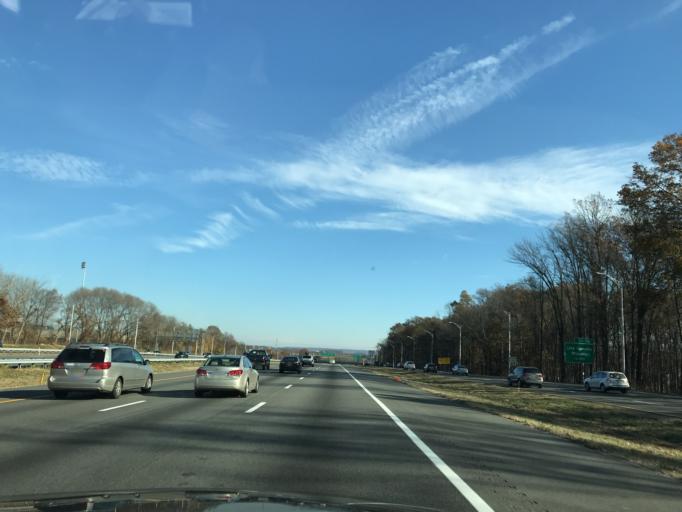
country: US
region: New Jersey
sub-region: Morris County
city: Parsippany
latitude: 40.8602
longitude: -74.3948
